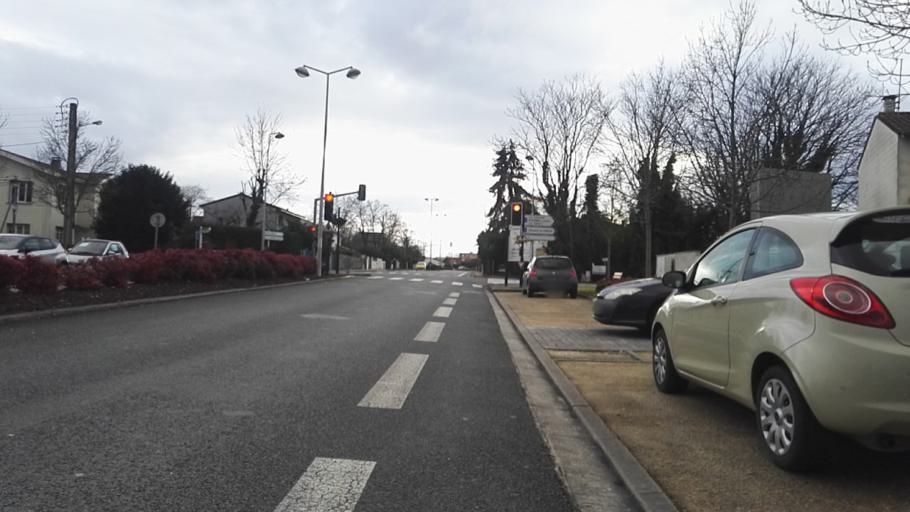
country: FR
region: Aquitaine
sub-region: Departement de la Gironde
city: Eysines
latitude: 44.8678
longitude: -0.6370
